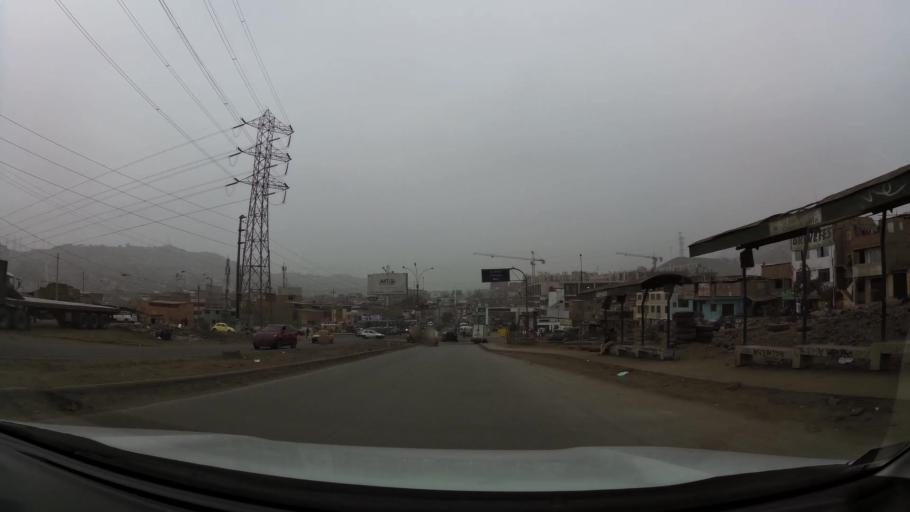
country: PE
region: Lima
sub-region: Lima
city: Surco
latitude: -12.1832
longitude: -76.9418
